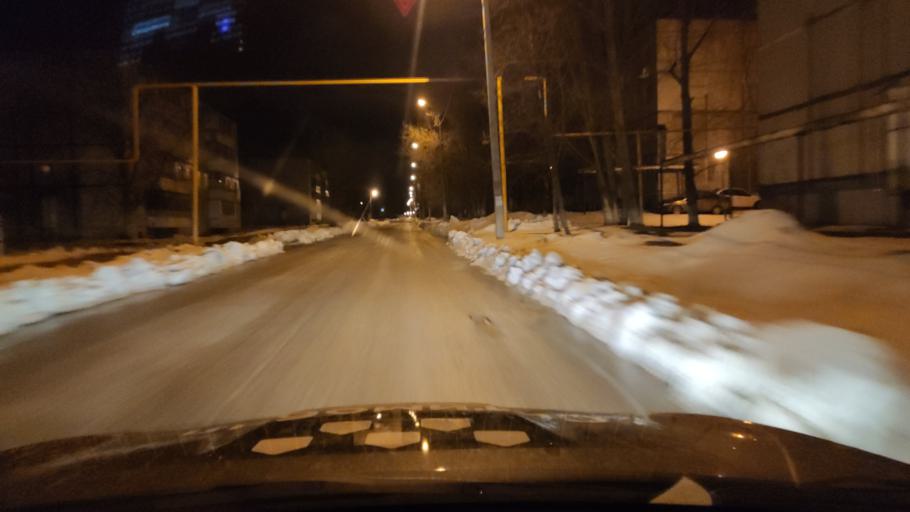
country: RU
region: Samara
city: Povolzhskiy
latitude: 53.5869
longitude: 49.7652
